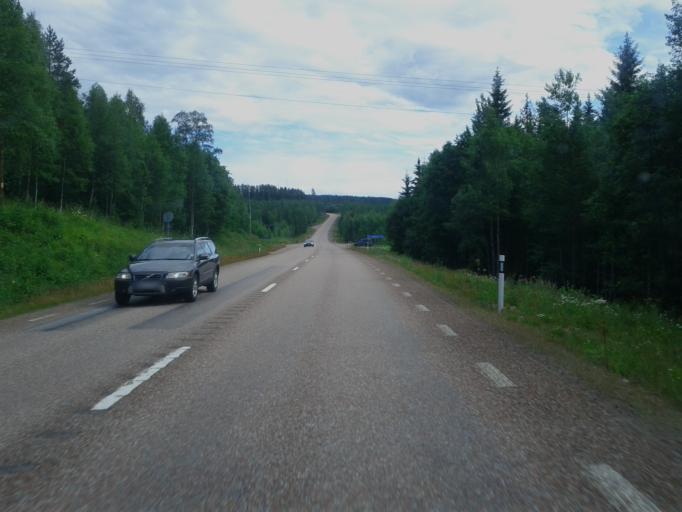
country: SE
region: Dalarna
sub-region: Rattviks Kommun
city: Raettvik
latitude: 60.7950
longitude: 15.2740
